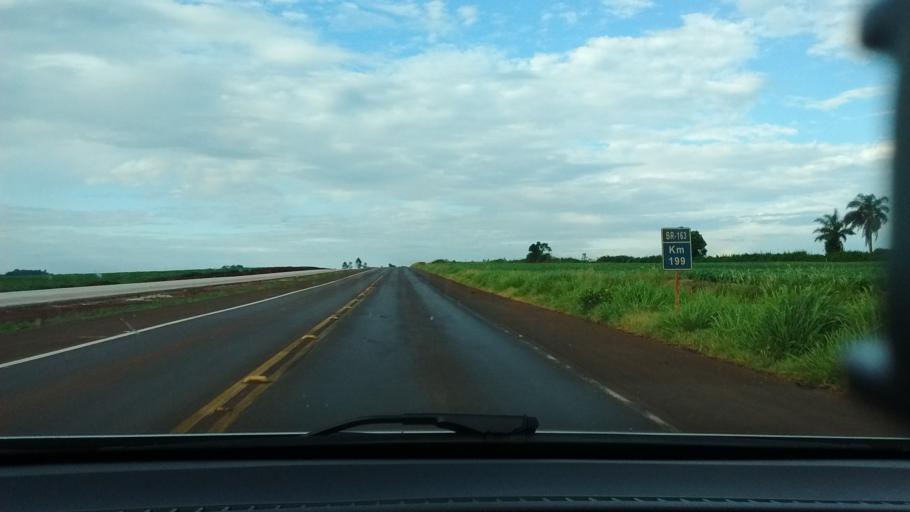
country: BR
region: Parana
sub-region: Cascavel
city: Cascavel
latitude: -25.0345
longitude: -53.5518
